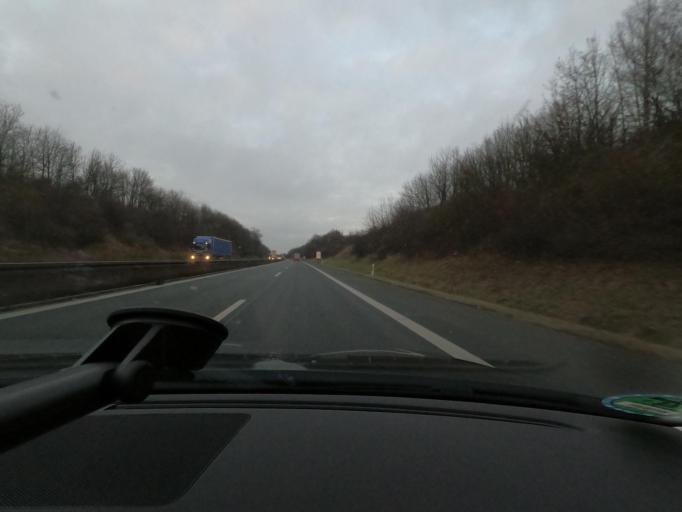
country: DE
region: Bavaria
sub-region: Upper Franconia
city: Hirschaid
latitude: 49.8349
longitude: 11.0053
